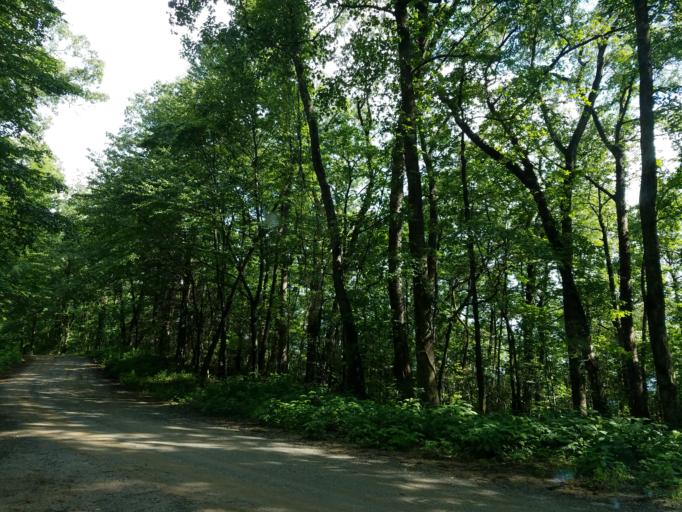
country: US
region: Georgia
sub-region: Fannin County
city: Blue Ridge
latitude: 34.6665
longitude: -84.2376
